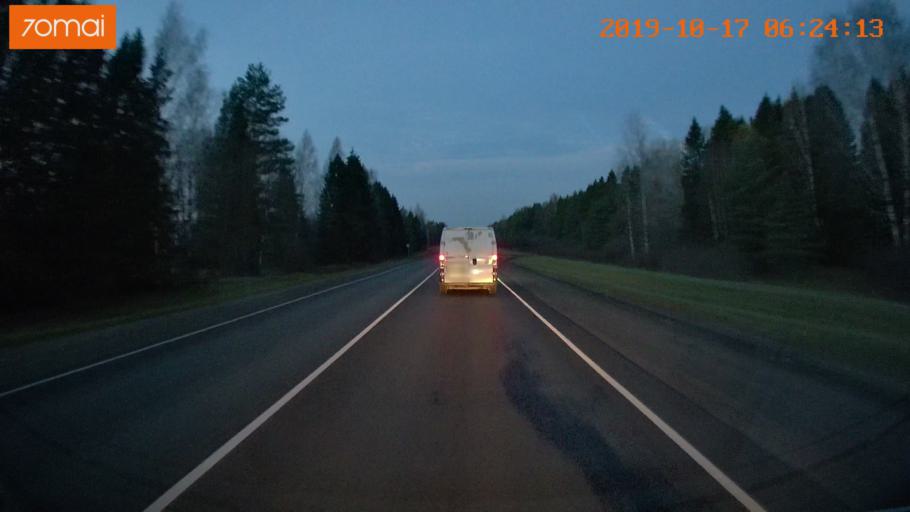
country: RU
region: Ivanovo
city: Lezhnevo
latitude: 56.7774
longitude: 40.8323
